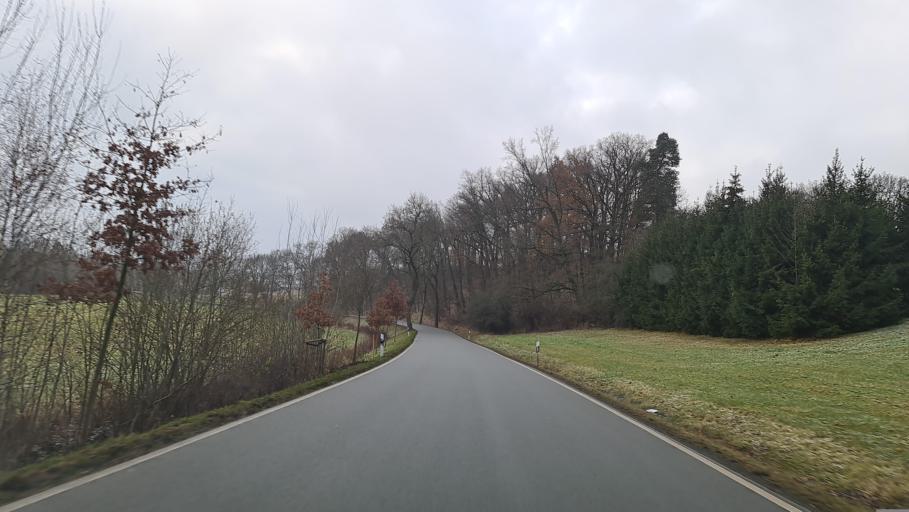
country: DE
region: Saxony
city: Weischlitz
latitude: 50.4696
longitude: 12.0710
